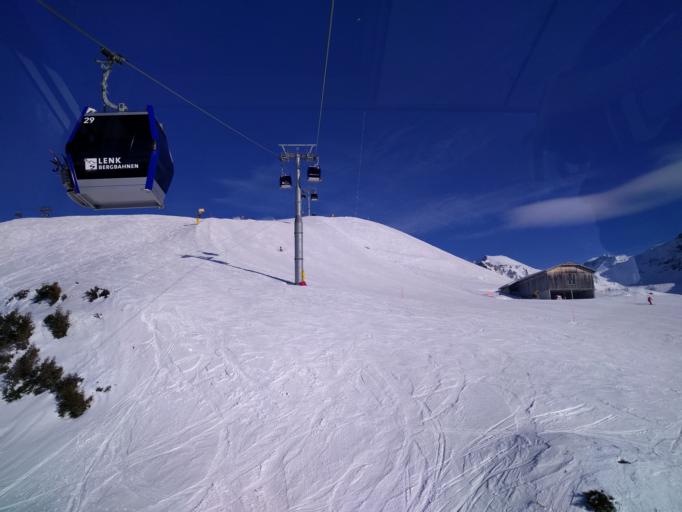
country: CH
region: Bern
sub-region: Obersimmental-Saanen District
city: Lenk
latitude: 46.4442
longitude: 7.4859
